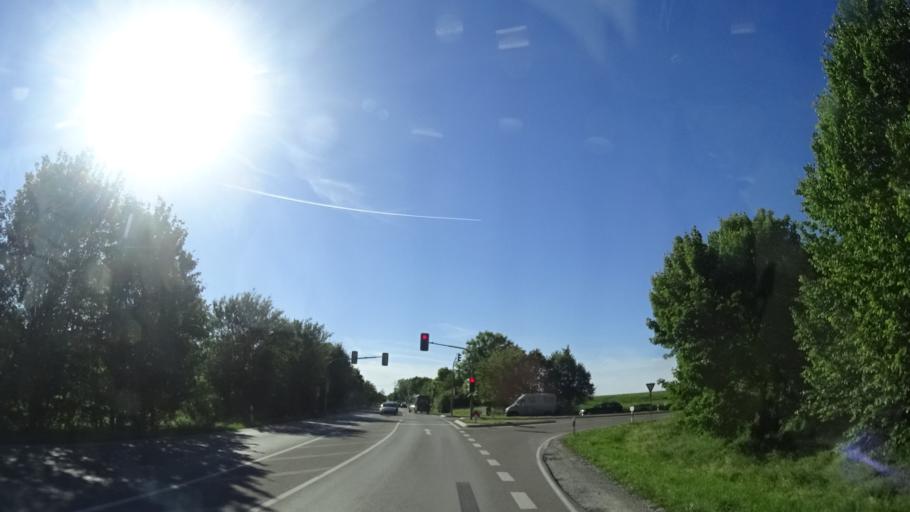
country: DE
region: Baden-Wuerttemberg
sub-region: Regierungsbezirk Stuttgart
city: Vellberg
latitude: 49.0832
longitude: 9.8677
